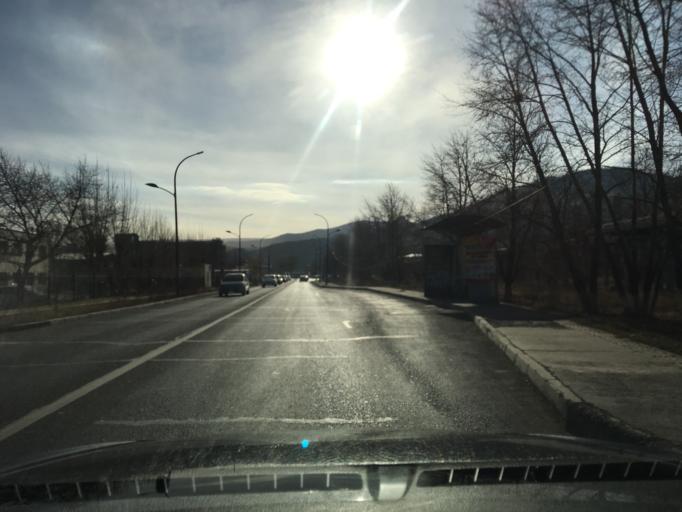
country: MN
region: Ulaanbaatar
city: Ulaanbaatar
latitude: 47.8952
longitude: 106.8737
